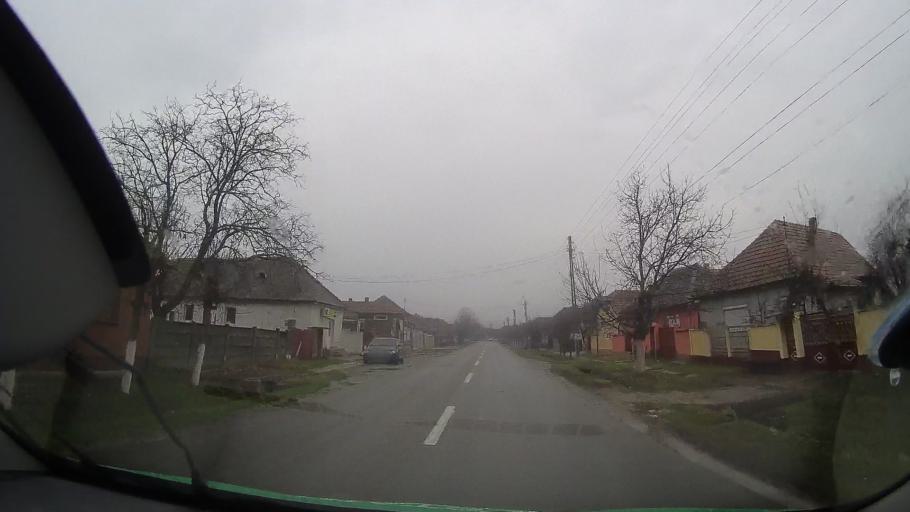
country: RO
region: Bihor
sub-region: Comuna Tulca
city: Tulca
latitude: 46.7899
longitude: 21.7731
